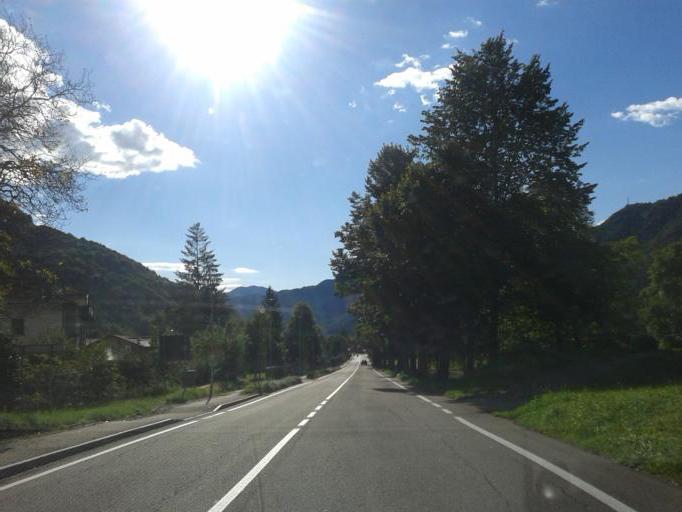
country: IT
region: Trentino-Alto Adige
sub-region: Provincia di Trento
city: Pieve di Ledro
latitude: 45.8927
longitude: 10.7246
